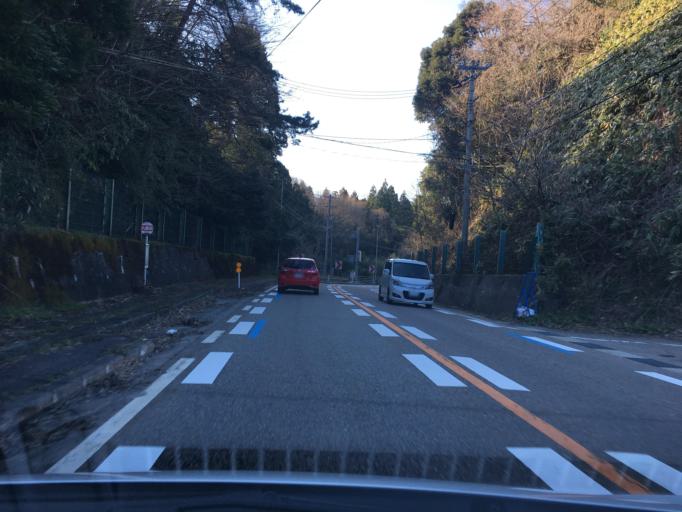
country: JP
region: Toyama
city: Himi
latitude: 36.9268
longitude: 137.0261
